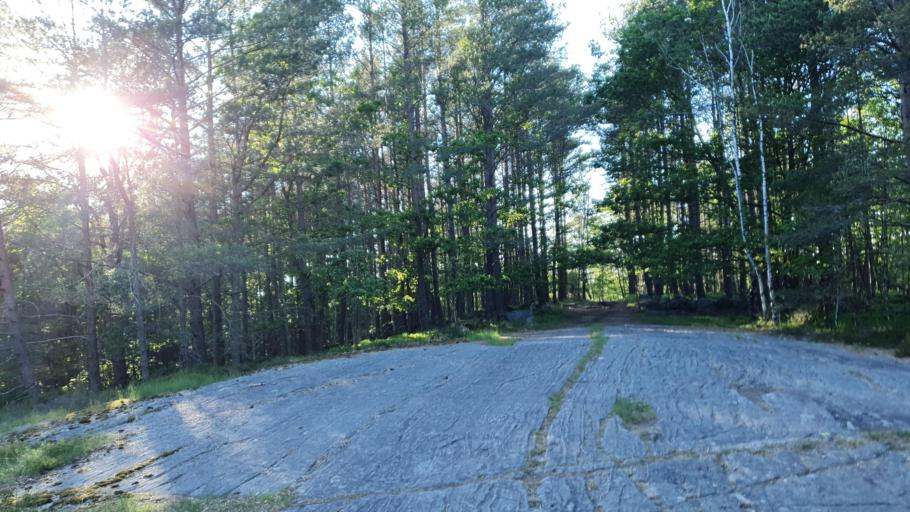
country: SE
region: Vaestra Goetaland
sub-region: Molndal
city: Kallered
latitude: 57.6370
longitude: 12.0538
